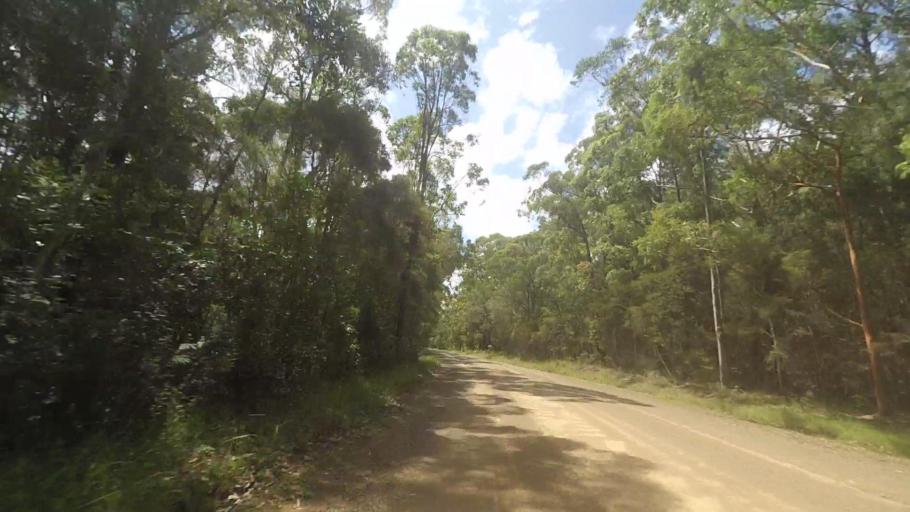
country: AU
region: New South Wales
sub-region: Great Lakes
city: Bulahdelah
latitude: -32.4920
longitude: 152.2760
